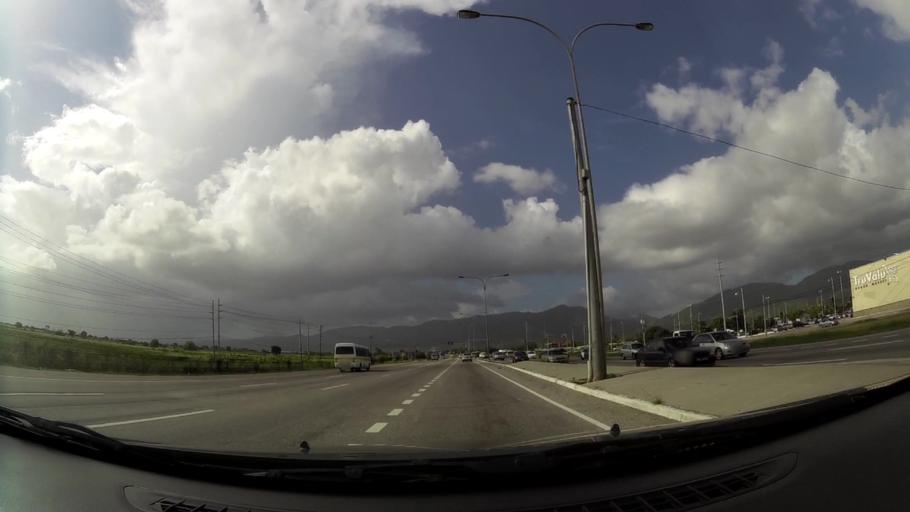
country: TT
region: Tunapuna/Piarco
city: Arouca
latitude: 10.6244
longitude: -61.3561
